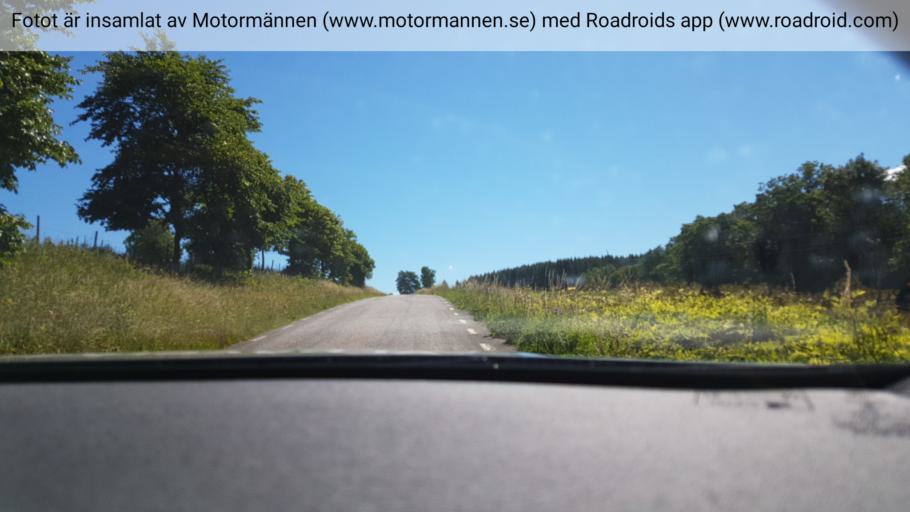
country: SE
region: Vaestra Goetaland
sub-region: Falkopings Kommun
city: Akarp
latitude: 58.1873
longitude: 13.7539
